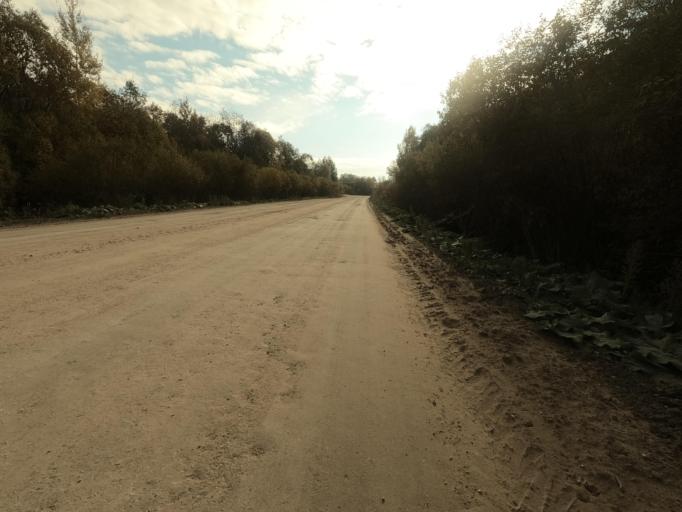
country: RU
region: Novgorod
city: Batetskiy
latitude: 58.8011
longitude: 30.6528
